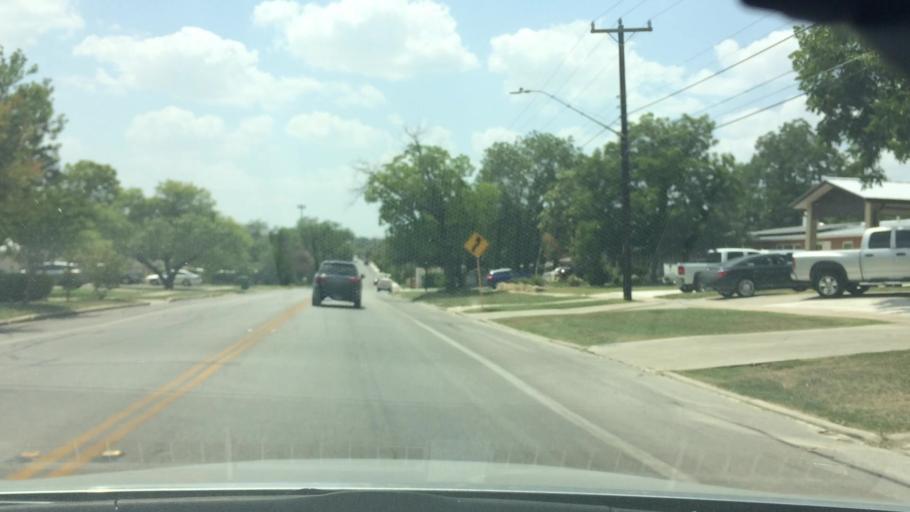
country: US
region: Texas
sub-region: Bexar County
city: Olmos Park
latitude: 29.5043
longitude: -98.4877
